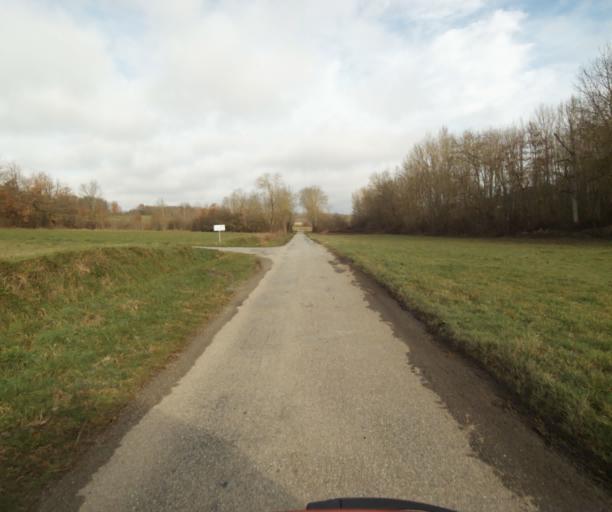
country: FR
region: Midi-Pyrenees
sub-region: Departement de l'Ariege
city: Saverdun
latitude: 43.1775
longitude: 1.5167
